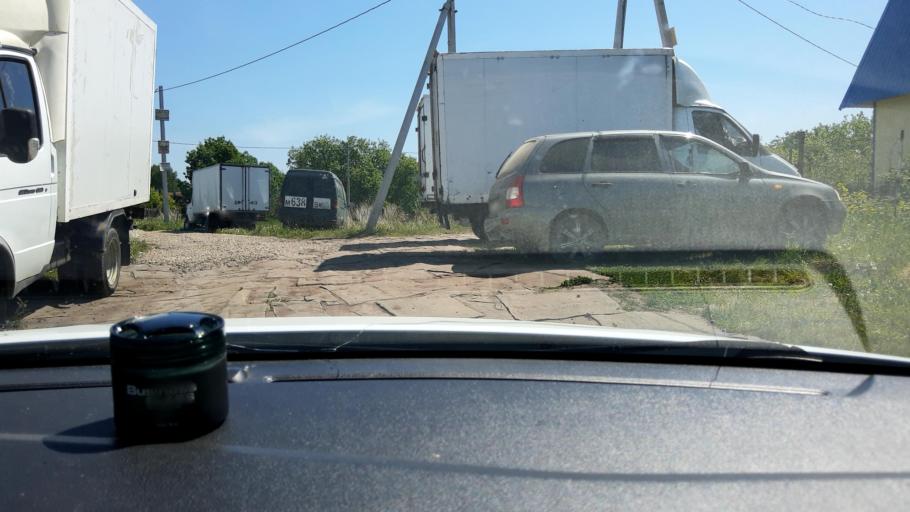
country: RU
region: Bashkortostan
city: Mikhaylovka
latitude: 54.8423
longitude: 55.9512
